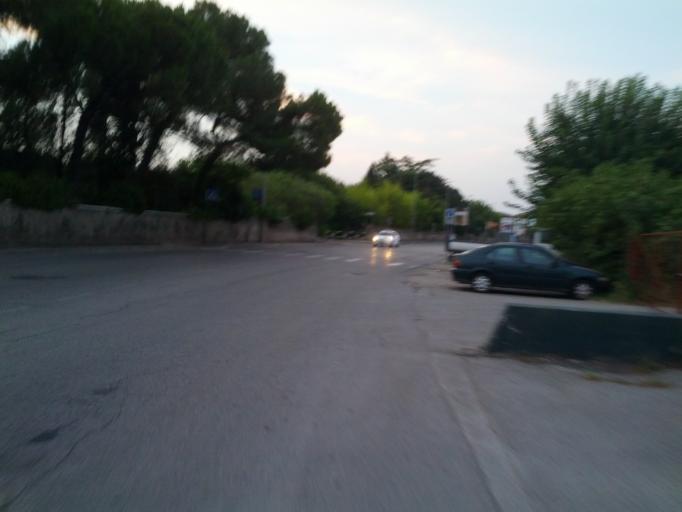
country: IT
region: Veneto
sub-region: Provincia di Verona
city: Verona
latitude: 45.4140
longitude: 10.9677
